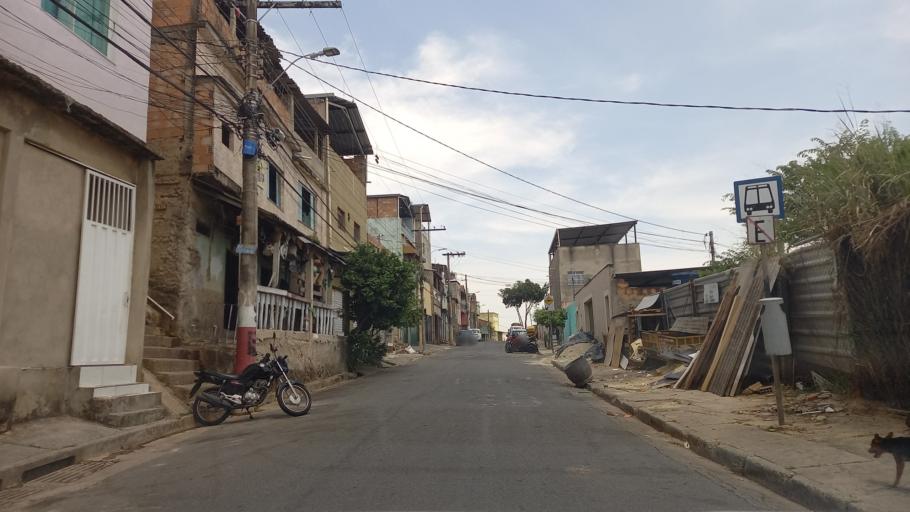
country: BR
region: Minas Gerais
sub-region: Contagem
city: Contagem
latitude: -19.9086
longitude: -44.0086
